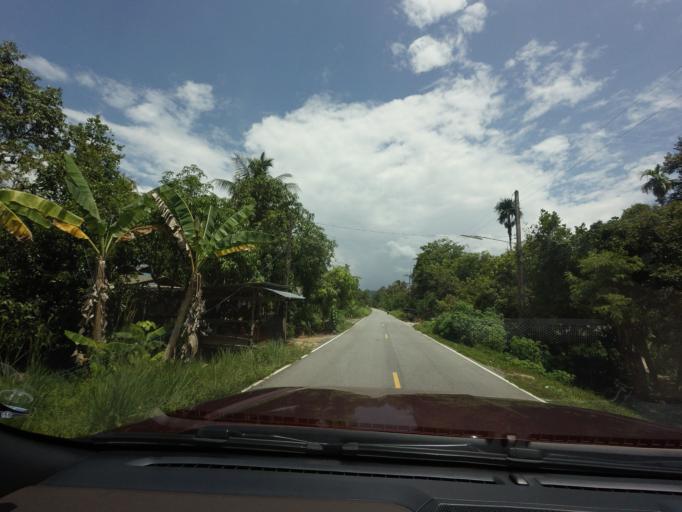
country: TH
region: Narathiwat
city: Chanae
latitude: 6.0823
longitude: 101.6897
